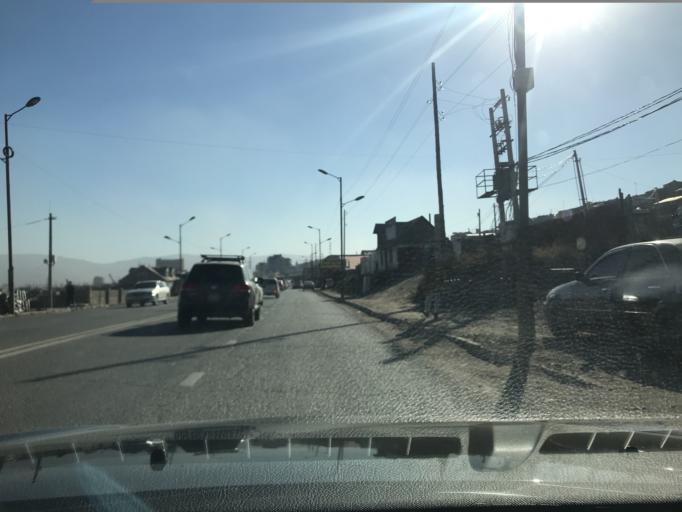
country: MN
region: Ulaanbaatar
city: Ulaanbaatar
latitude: 47.9738
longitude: 106.9179
